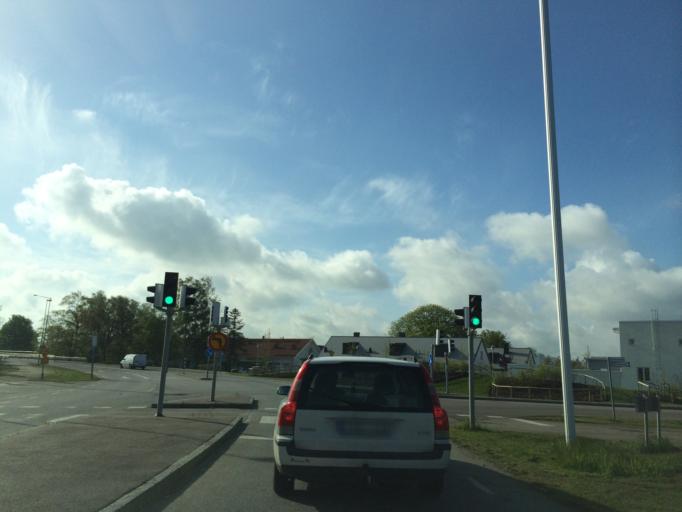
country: SE
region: Skane
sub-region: Lomma Kommun
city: Lomma
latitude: 55.6812
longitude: 13.0678
